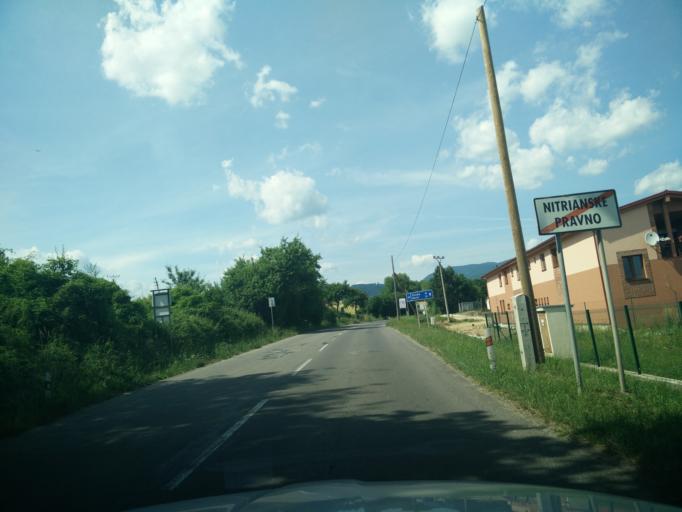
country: SK
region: Nitriansky
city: Prievidza
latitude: 48.8780
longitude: 18.6379
